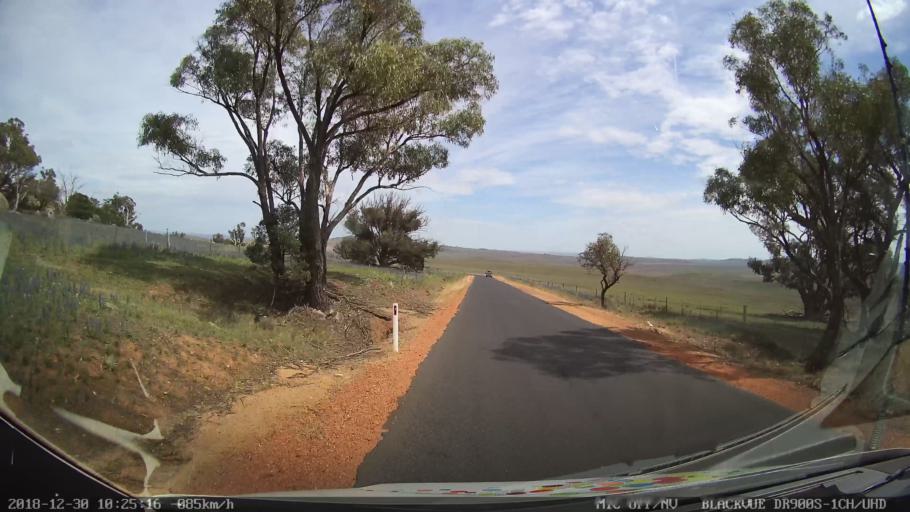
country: AU
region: New South Wales
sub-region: Snowy River
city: Berridale
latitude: -36.5263
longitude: 148.9603
